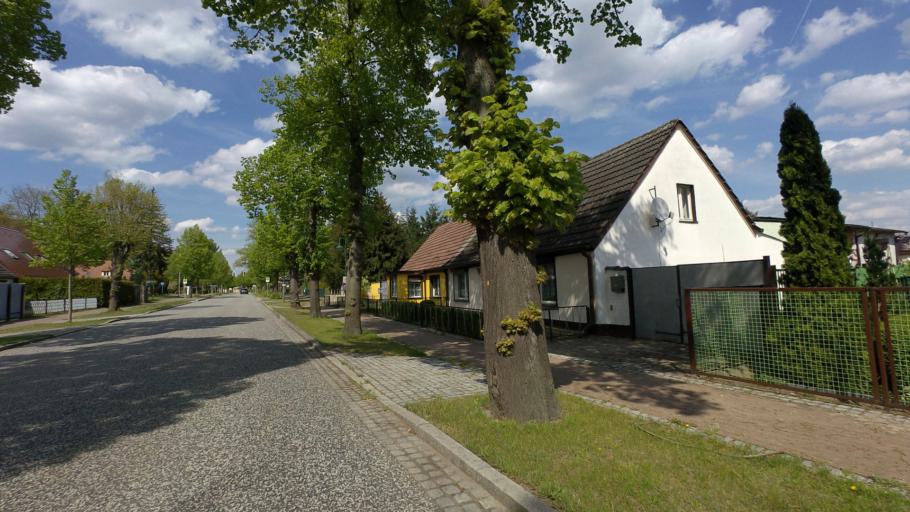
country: DE
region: Brandenburg
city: Marienwerder
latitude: 52.9001
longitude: 13.5363
